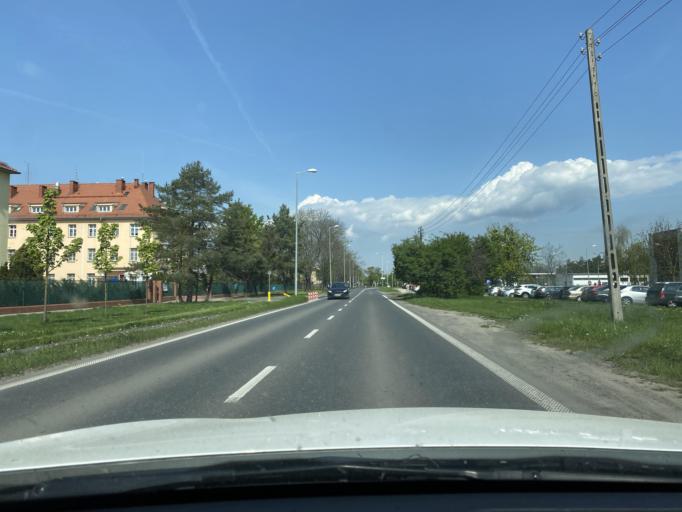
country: PL
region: Lower Silesian Voivodeship
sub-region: Powiat trzebnicki
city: Psary
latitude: 51.1459
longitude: 17.0225
